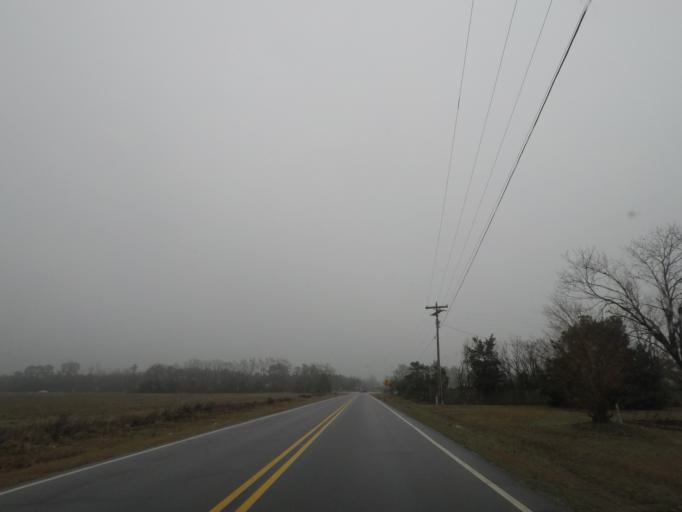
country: US
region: North Carolina
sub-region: Scotland County
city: Laurinburg
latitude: 34.8053
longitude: -79.4399
